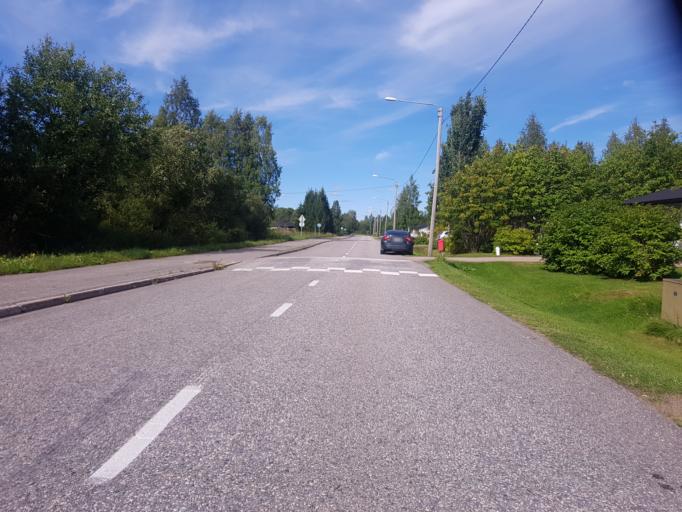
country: FI
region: Kainuu
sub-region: Kehys-Kainuu
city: Kuhmo
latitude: 64.1232
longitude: 29.5455
